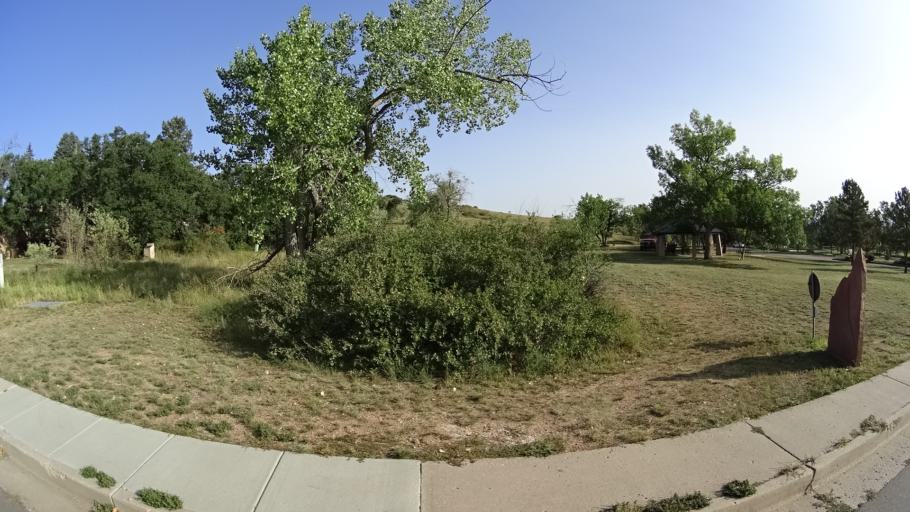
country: US
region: Colorado
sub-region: El Paso County
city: Colorado Springs
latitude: 38.8204
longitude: -104.8636
